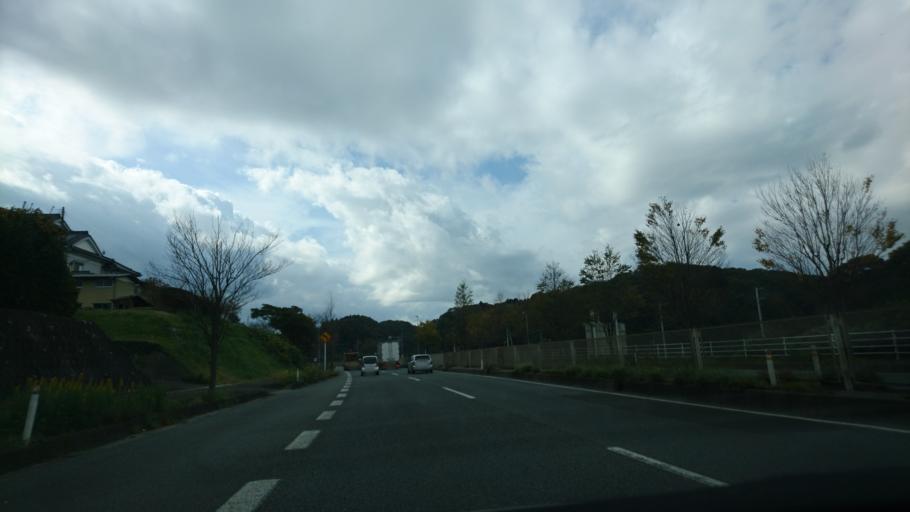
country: JP
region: Miyagi
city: Tomiya
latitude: 38.3826
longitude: 140.8738
